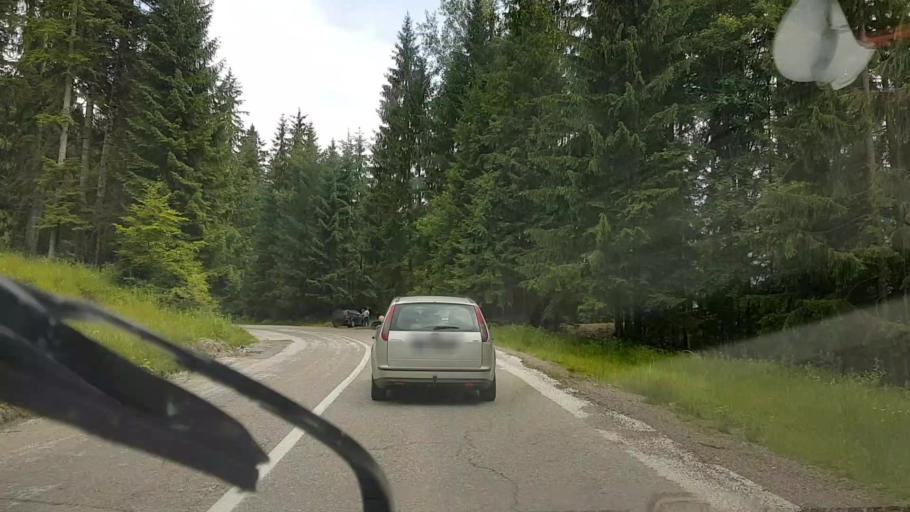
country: RO
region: Neamt
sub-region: Comuna Pangarati
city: Pangarati
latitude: 46.9717
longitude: 26.1171
